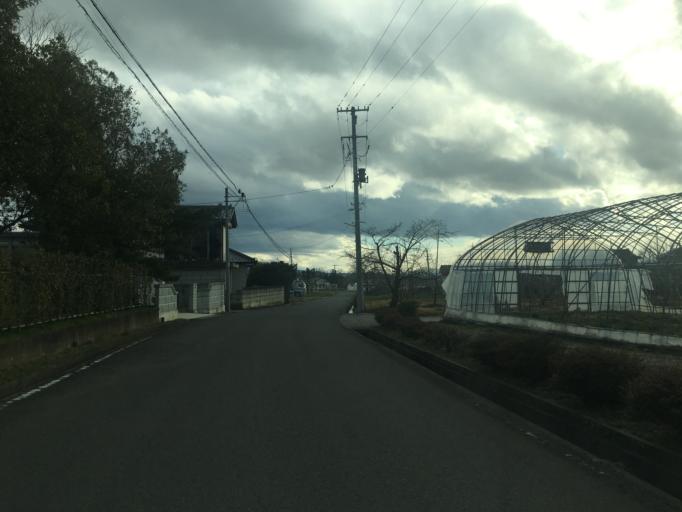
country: JP
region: Fukushima
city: Yanagawamachi-saiwaicho
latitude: 37.8794
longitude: 140.5747
